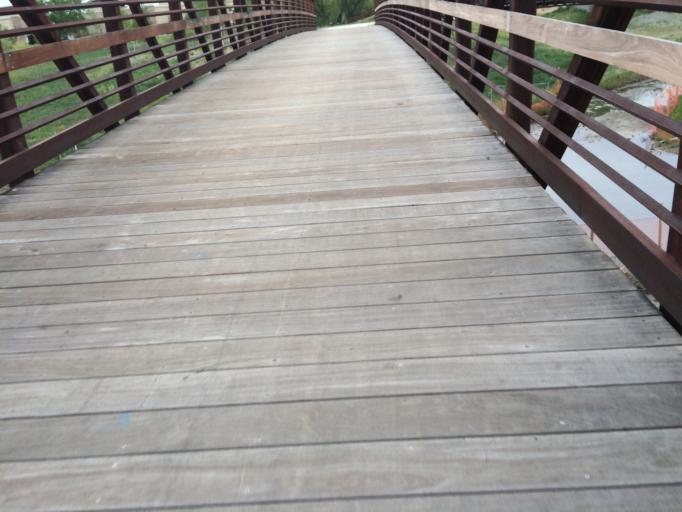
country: US
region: Colorado
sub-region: Boulder County
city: Longmont
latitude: 40.1552
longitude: -105.1001
